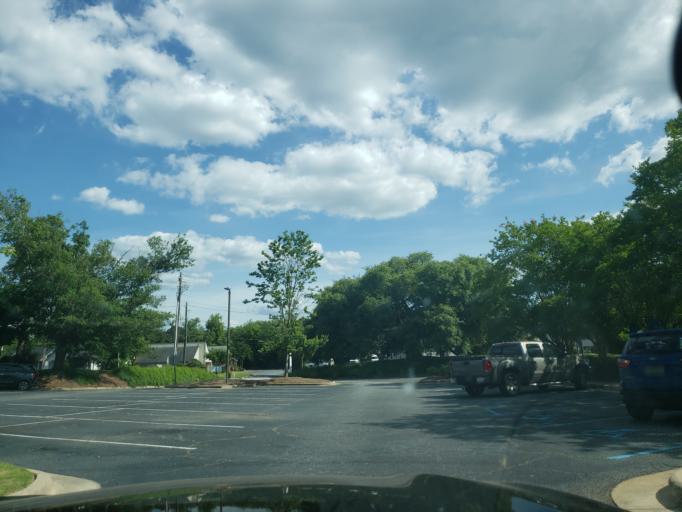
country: US
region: Georgia
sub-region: Muscogee County
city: Columbus
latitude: 32.4672
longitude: -84.9736
